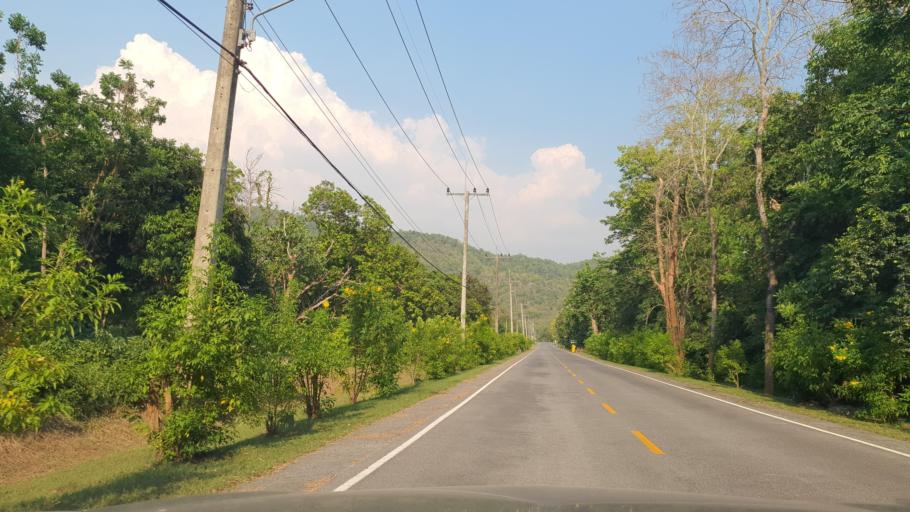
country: TH
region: Kanchanaburi
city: Sai Yok
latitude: 14.2299
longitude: 99.2321
